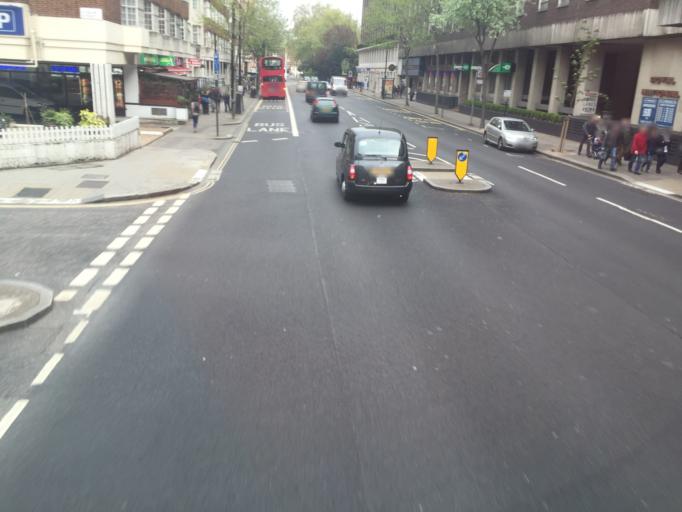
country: GB
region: England
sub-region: Greater London
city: London
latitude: 51.5240
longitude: -0.1270
